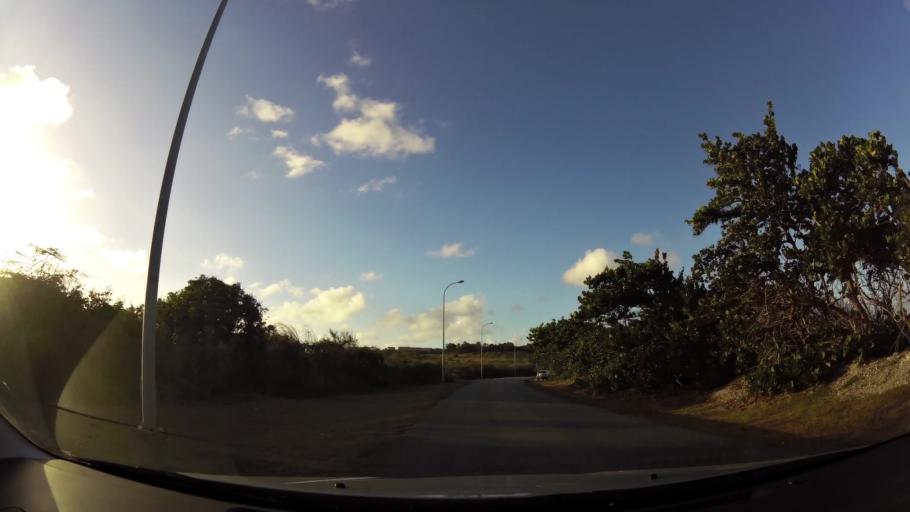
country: AG
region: Saint George
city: Piggotts
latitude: 17.1629
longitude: -61.7992
